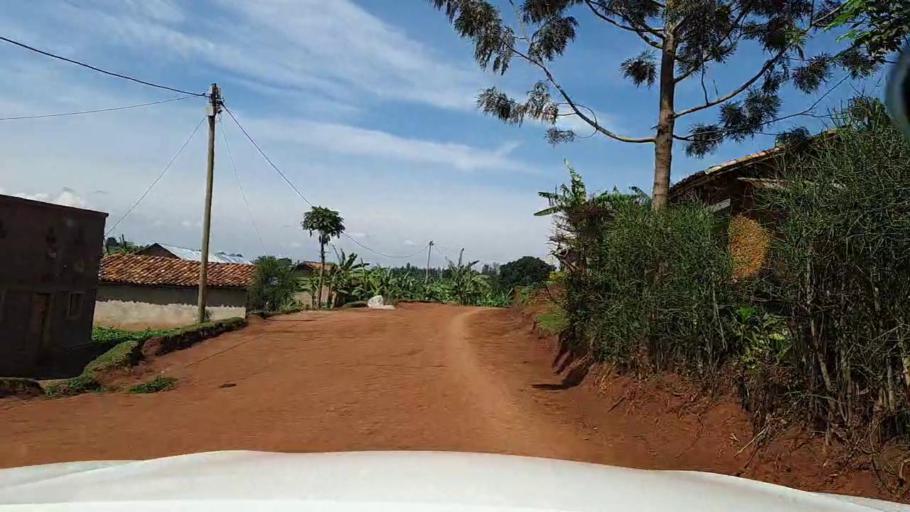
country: RW
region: Southern Province
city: Butare
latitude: -2.7054
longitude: 29.8443
